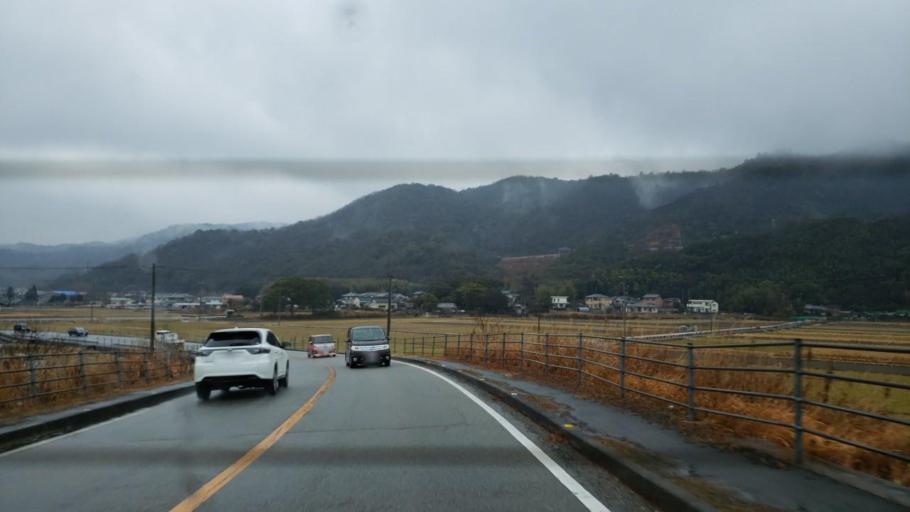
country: JP
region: Tokushima
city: Narutocho-mitsuishi
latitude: 34.1617
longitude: 134.5540
